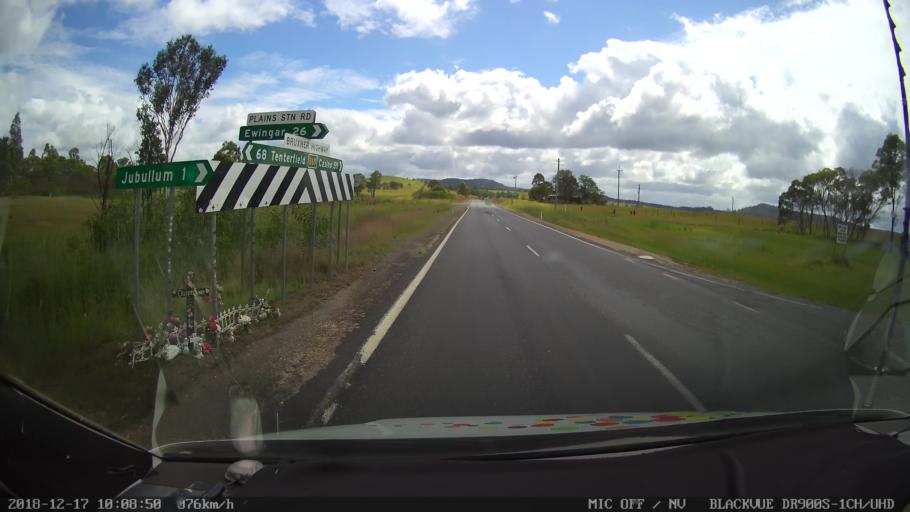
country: AU
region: New South Wales
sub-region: Tenterfield Municipality
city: Carrolls Creek
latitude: -28.8895
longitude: 152.5365
